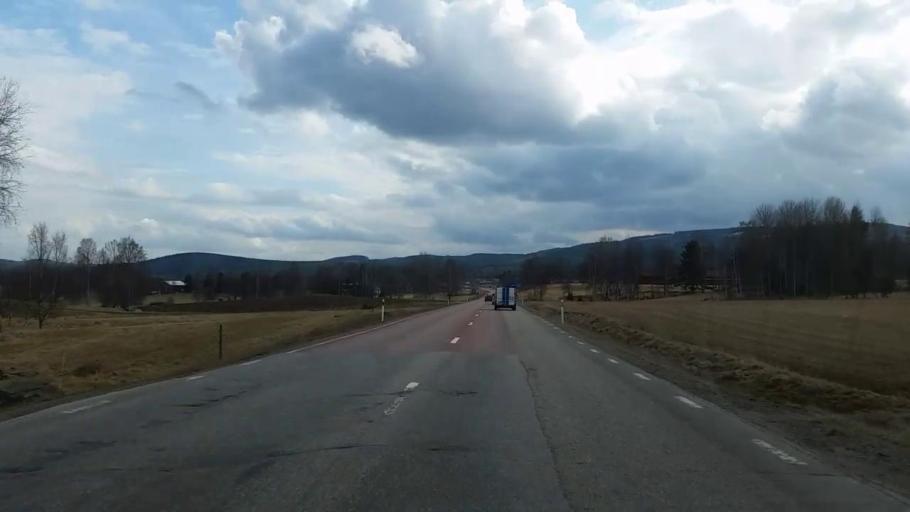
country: SE
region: Gaevleborg
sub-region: Ljusdals Kommun
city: Jaervsoe
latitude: 61.6798
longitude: 16.1454
